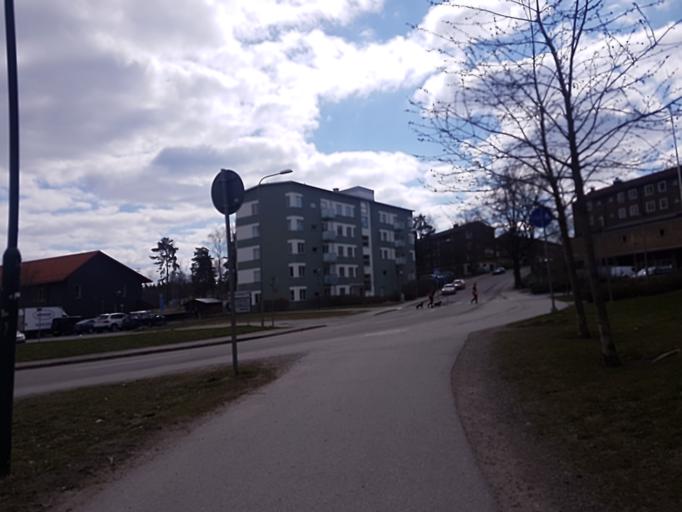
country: SE
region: Stockholm
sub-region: Nacka Kommun
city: Nacka
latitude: 59.2870
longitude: 18.1180
